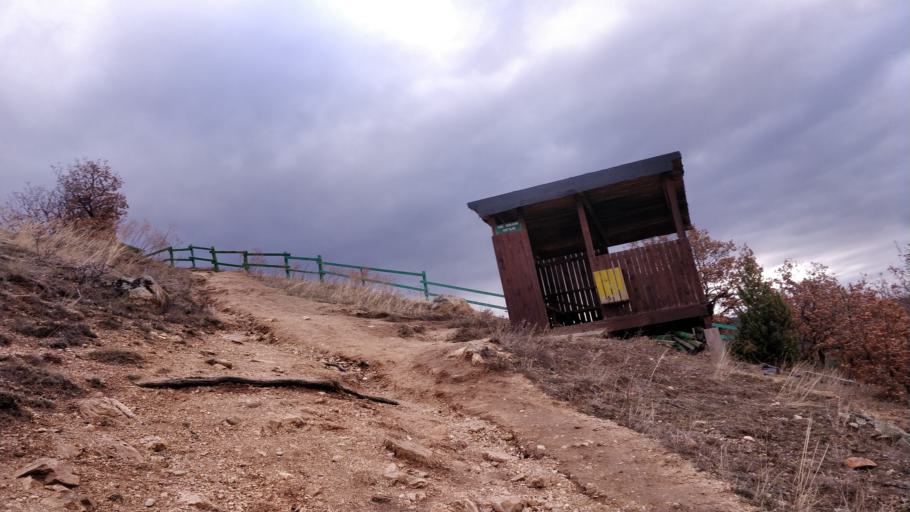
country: BG
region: Kyustendil
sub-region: Obshtina Rila
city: Rila
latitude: 42.0930
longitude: 23.1182
